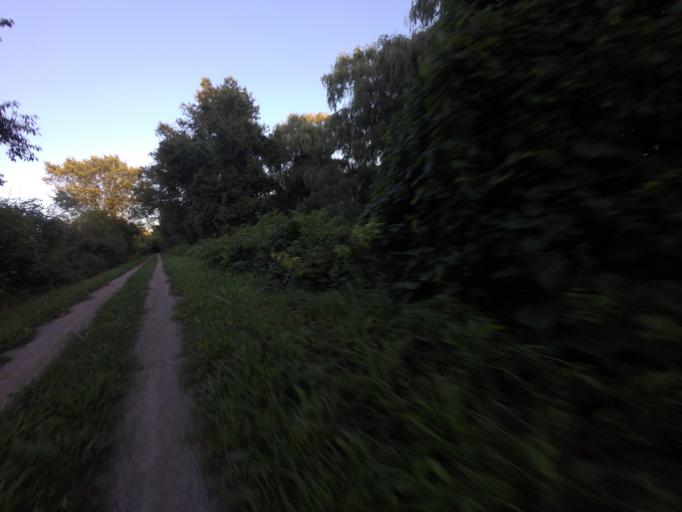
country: CA
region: Ontario
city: Goderich
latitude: 43.7485
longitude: -81.6491
